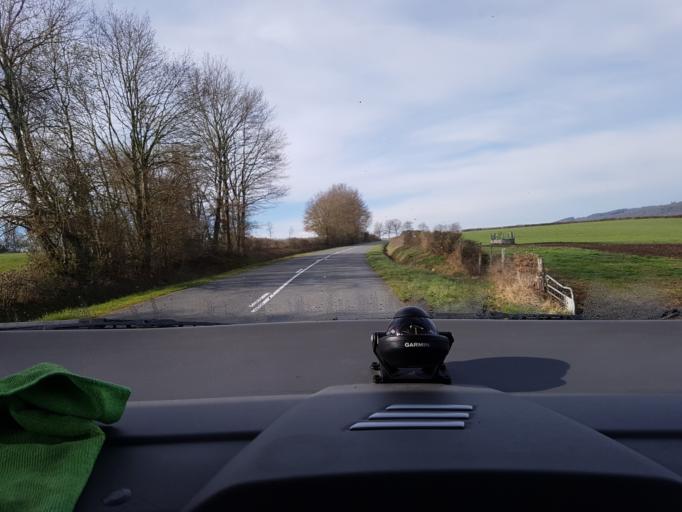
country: FR
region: Bourgogne
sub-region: Departement de Saone-et-Loire
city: Toulon-sur-Arroux
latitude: 46.7654
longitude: 4.1378
